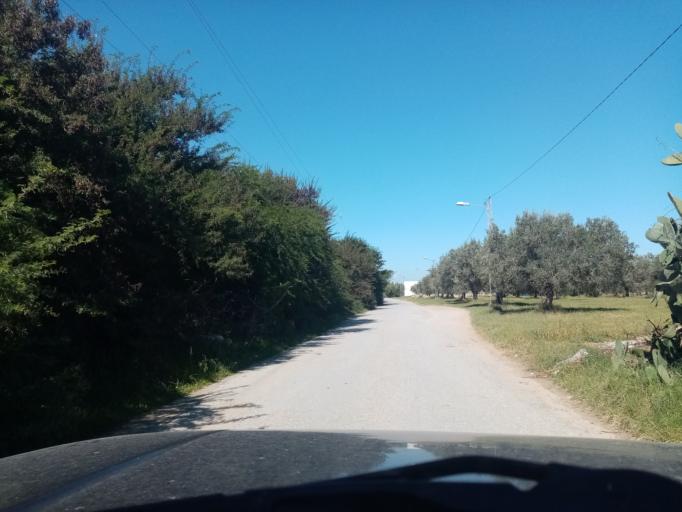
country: TN
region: Nabul
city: Bu `Urqub
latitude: 36.5685
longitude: 10.5789
